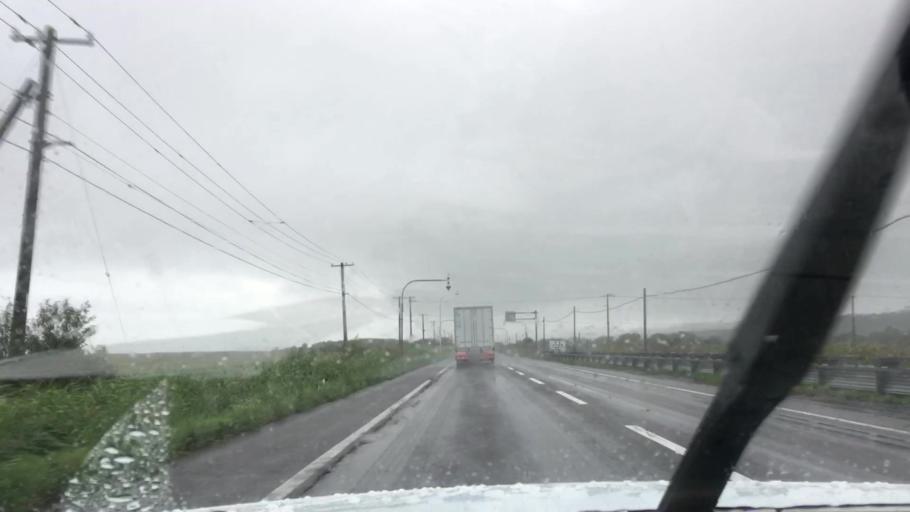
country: JP
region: Hokkaido
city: Niseko Town
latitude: 42.4250
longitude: 140.3154
